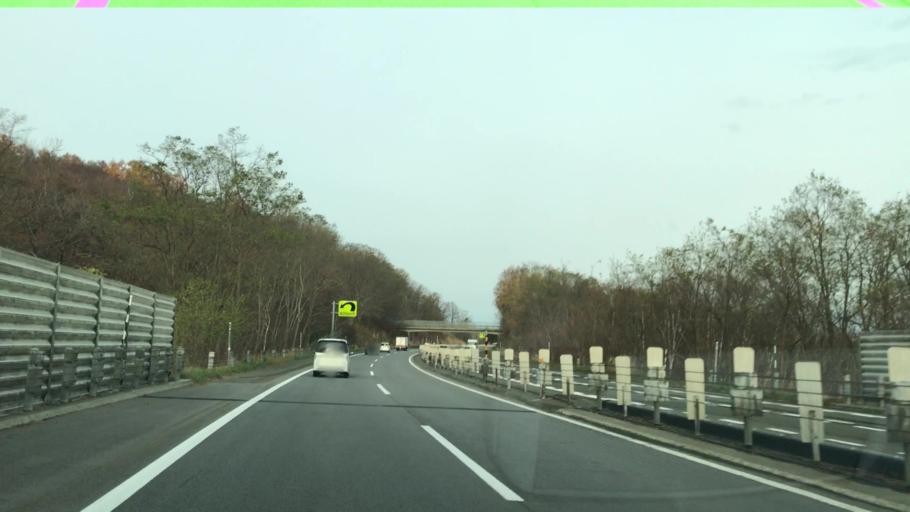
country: JP
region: Hokkaido
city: Otaru
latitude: 43.1471
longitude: 141.1328
